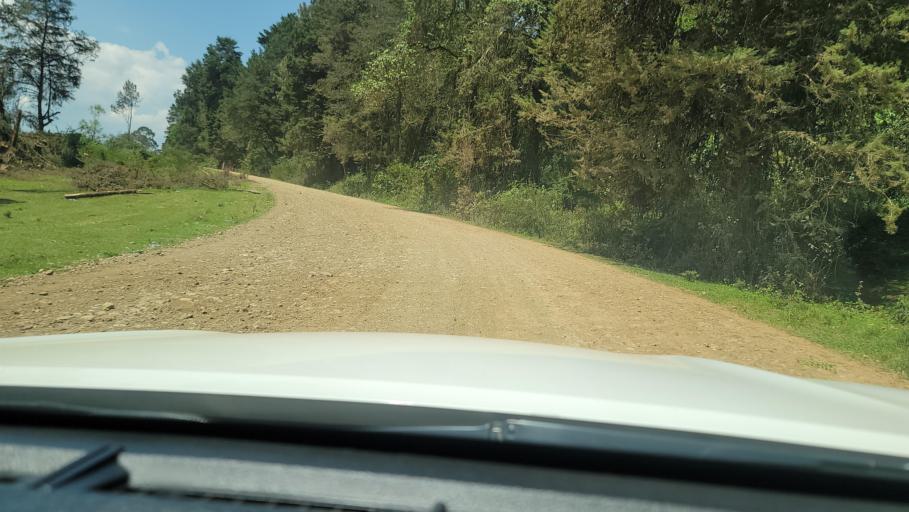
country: ET
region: Oromiya
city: Agaro
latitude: 7.7913
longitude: 36.4311
